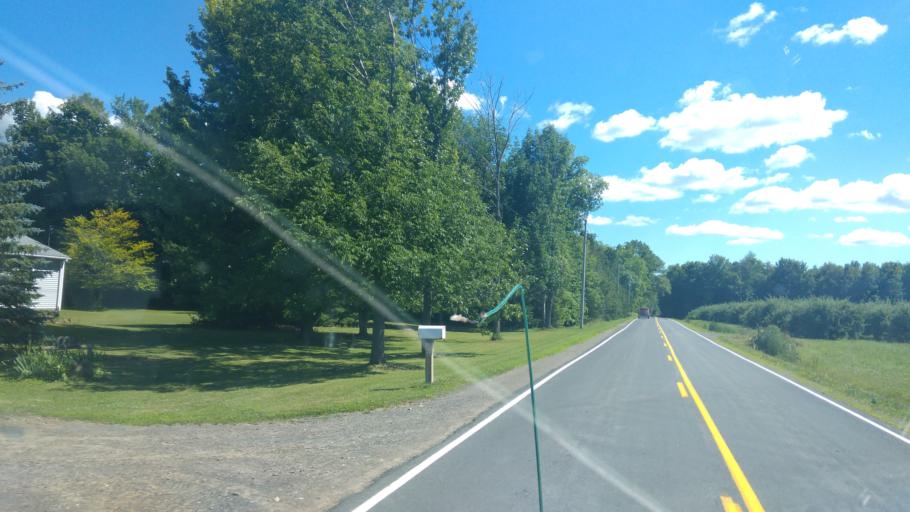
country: US
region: New York
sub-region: Wayne County
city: Sodus
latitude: 43.1975
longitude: -77.0494
